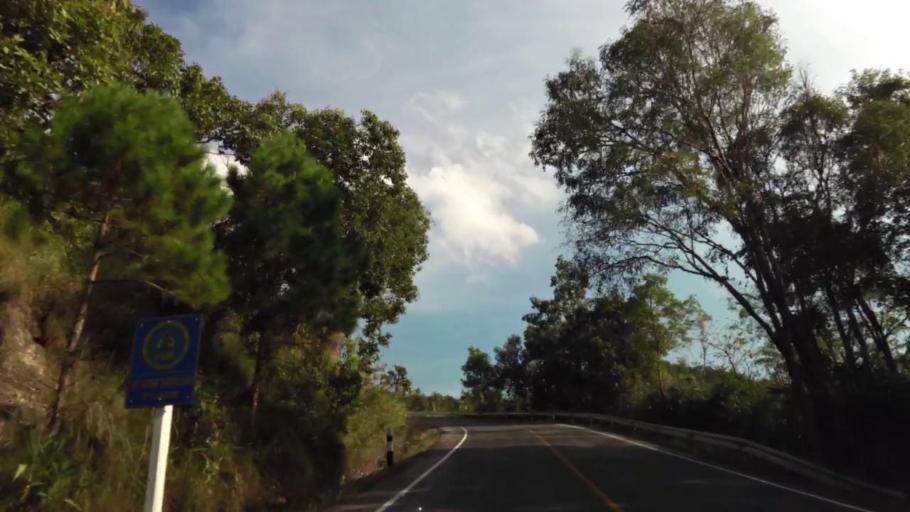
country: TH
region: Chiang Rai
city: Khun Tan
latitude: 19.8757
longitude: 100.3185
